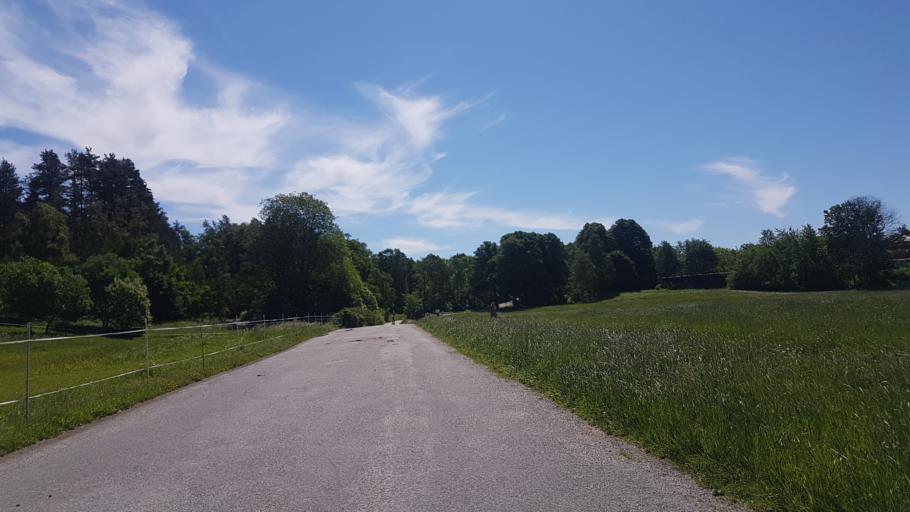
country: SE
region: Stockholm
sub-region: Lidingo
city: Lidingoe
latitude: 59.3348
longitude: 18.1215
